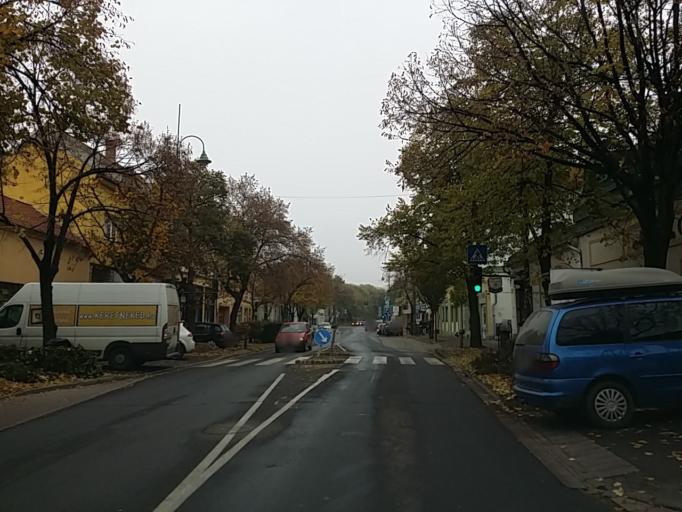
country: HU
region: Heves
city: Gyongyos
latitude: 47.7851
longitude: 19.9290
